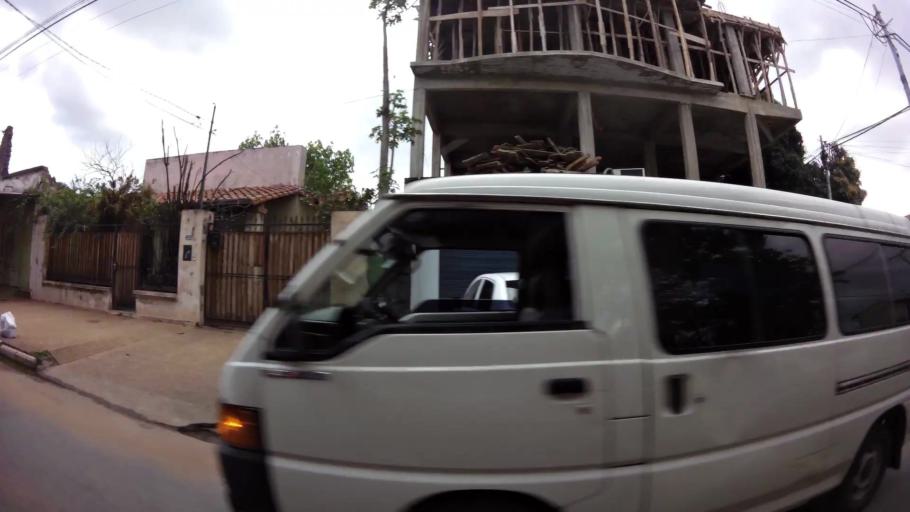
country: PY
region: Central
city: Fernando de la Mora
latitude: -25.3308
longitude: -57.5521
